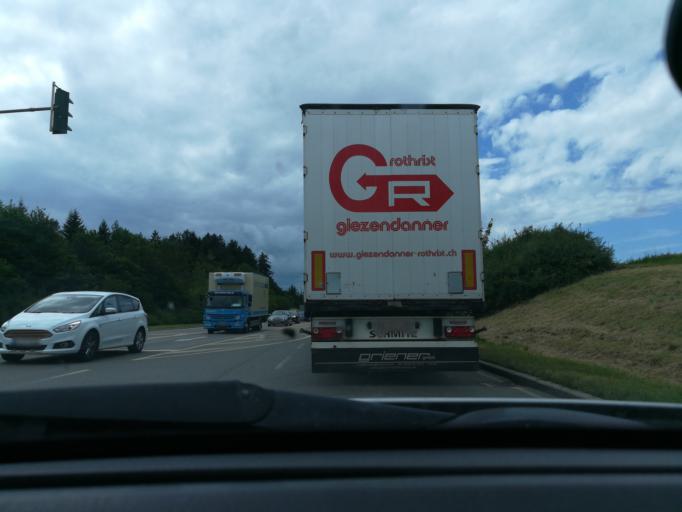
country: DE
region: Baden-Wuerttemberg
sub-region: Freiburg Region
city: Villingendorf
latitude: 48.1784
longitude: 8.5695
